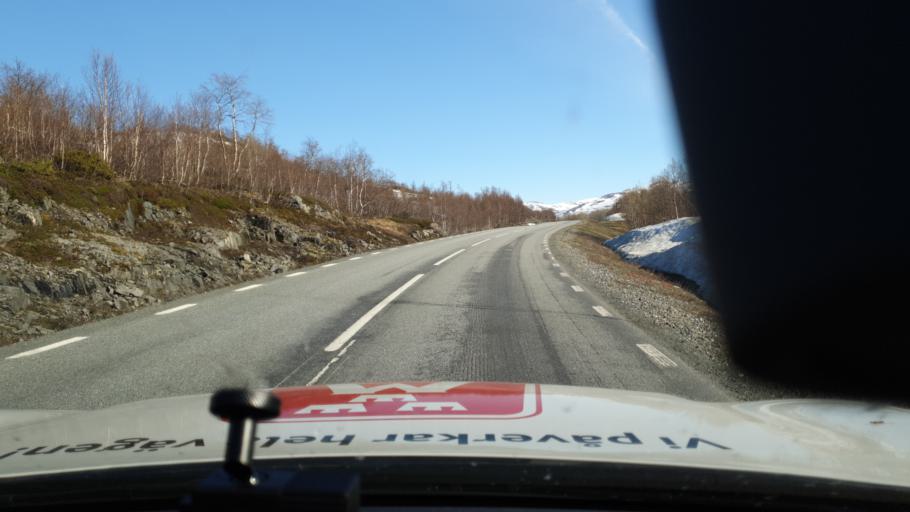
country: NO
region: Nordland
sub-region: Rana
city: Mo i Rana
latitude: 66.1310
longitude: 14.5992
